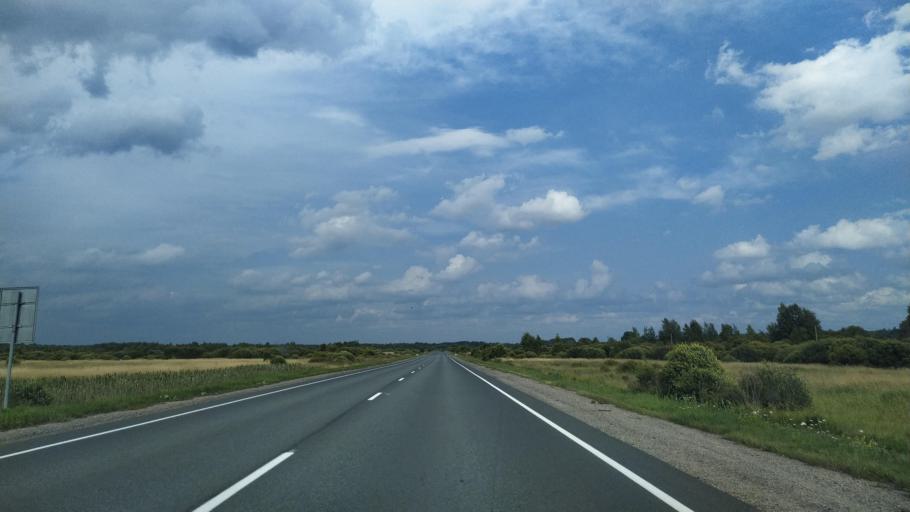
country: RU
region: Pskov
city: Porkhov
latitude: 57.9677
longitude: 29.6862
